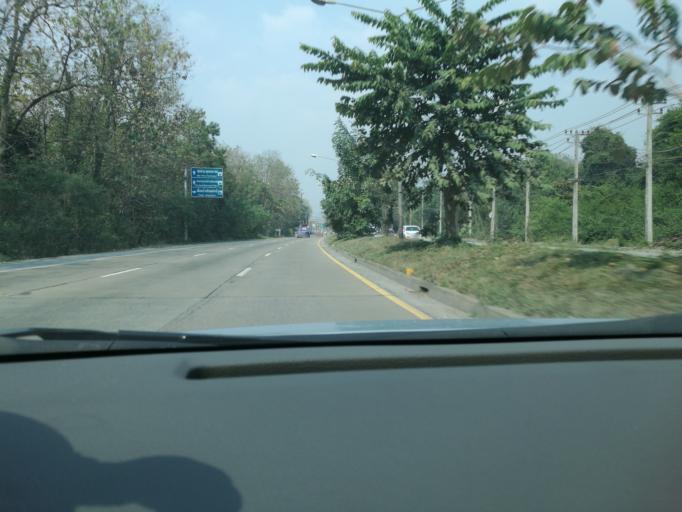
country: TH
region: Sara Buri
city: Chaloem Phra Kiat
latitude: 14.6819
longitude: 100.8745
